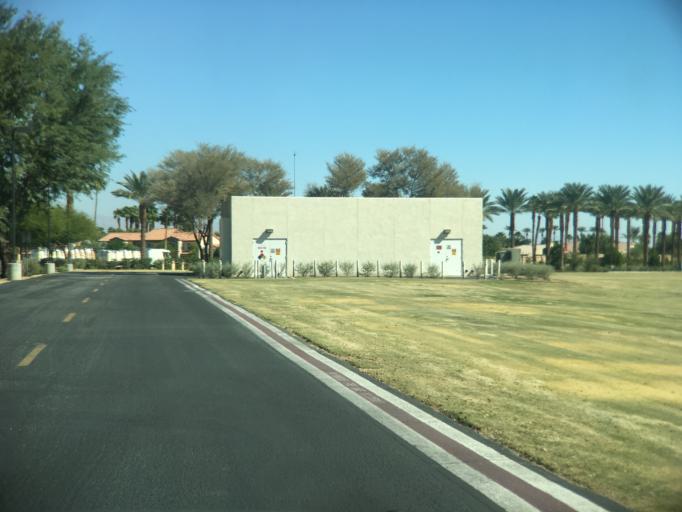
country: US
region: California
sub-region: Riverside County
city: Bermuda Dunes
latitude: 33.7264
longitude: -116.3048
